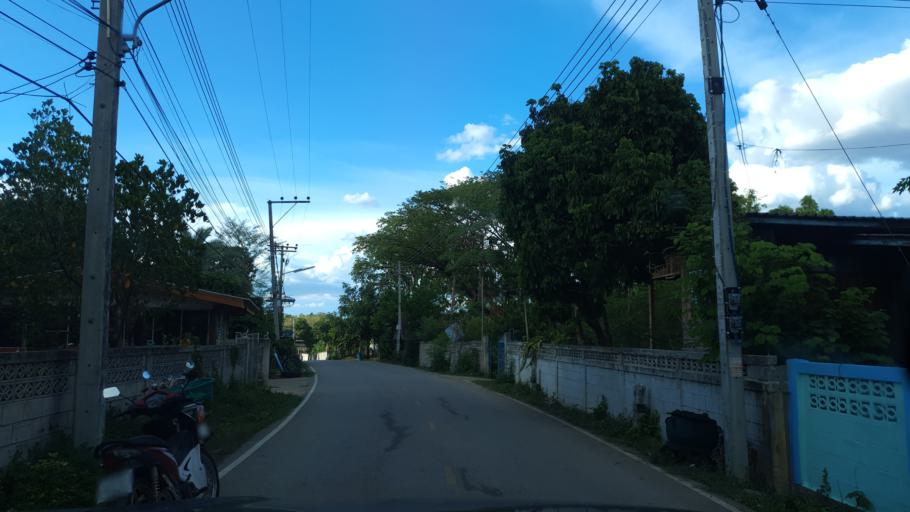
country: TH
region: Lampang
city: Sop Prap
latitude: 17.8704
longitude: 99.3080
